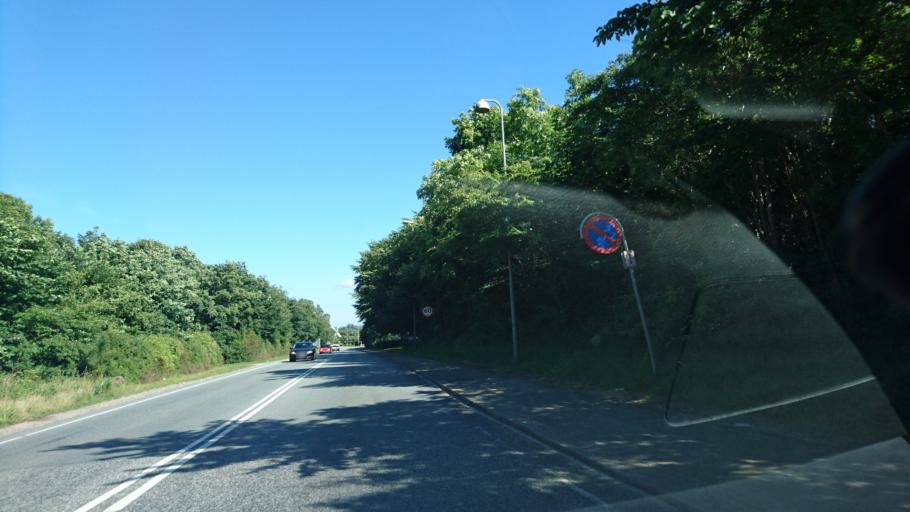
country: DK
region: North Denmark
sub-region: Alborg Kommune
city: Gistrup
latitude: 57.0439
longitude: 9.9735
